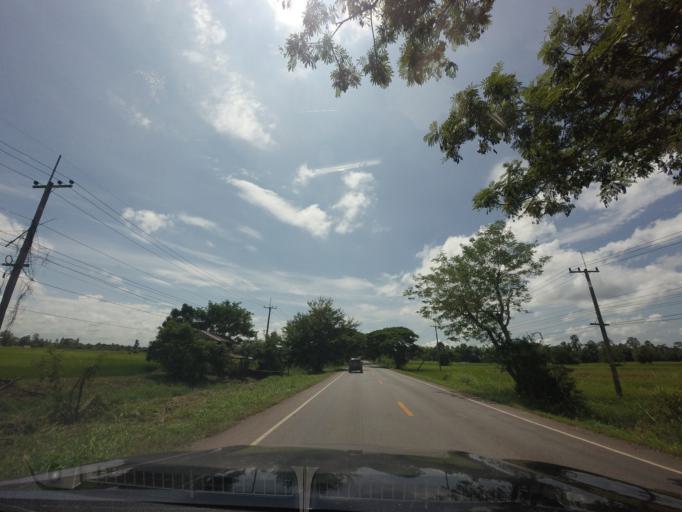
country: TH
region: Changwat Udon Thani
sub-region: Amphoe Ban Phue
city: Ban Phue
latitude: 17.7593
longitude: 102.3977
